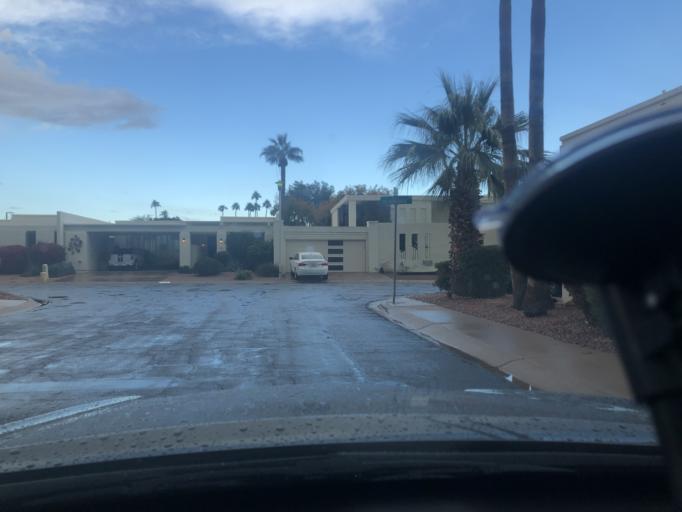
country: US
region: Arizona
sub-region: Maricopa County
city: Scottsdale
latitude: 33.4958
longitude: -111.8955
